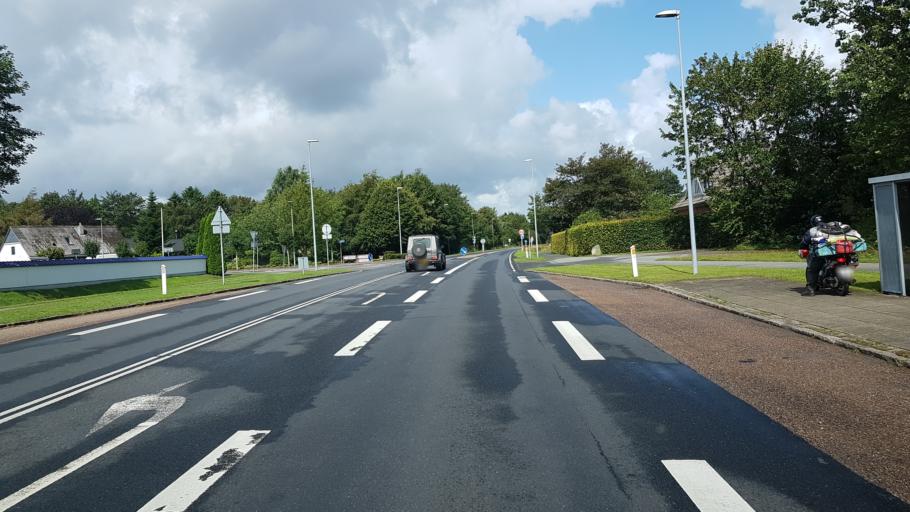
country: DK
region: South Denmark
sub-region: Vejen Kommune
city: Vejen
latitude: 55.5226
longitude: 9.1174
